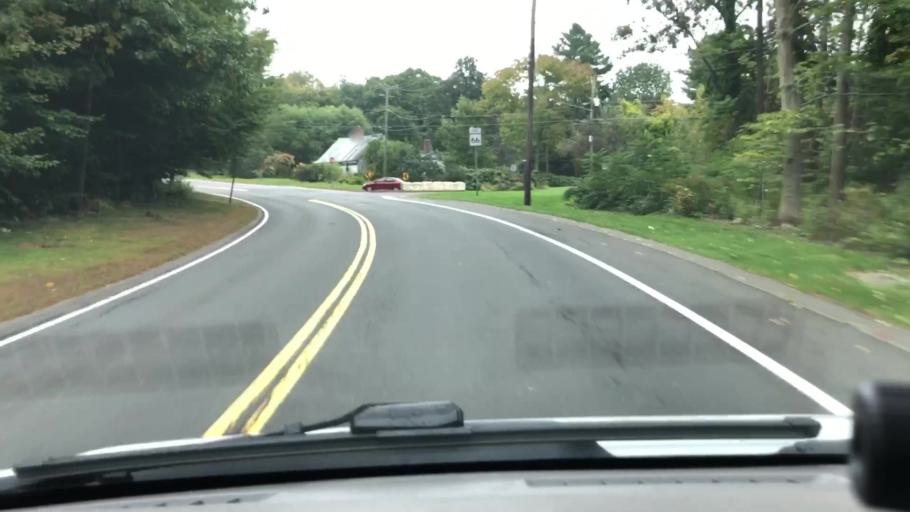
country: US
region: Massachusetts
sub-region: Hampshire County
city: Westhampton
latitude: 42.2818
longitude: -72.8256
